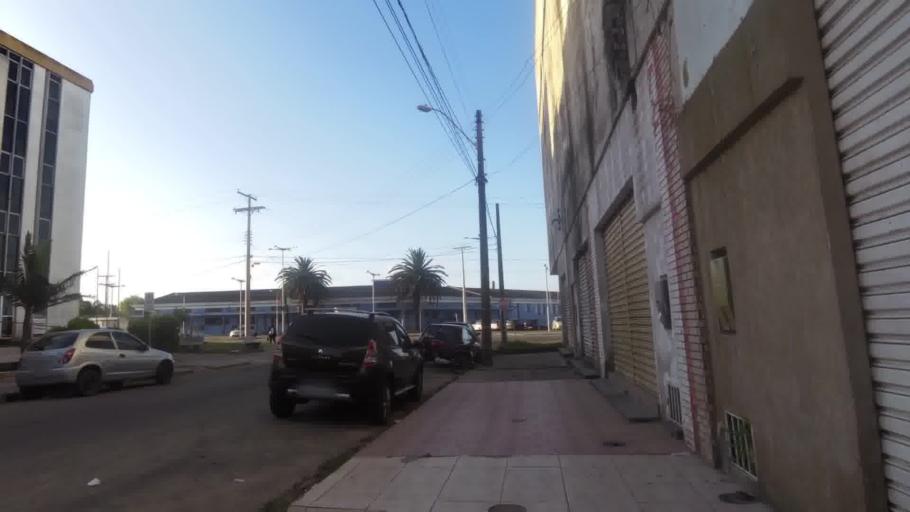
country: BR
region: Rio Grande do Sul
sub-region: Rio Grande
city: Rio Grande
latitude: -32.0289
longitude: -52.1023
